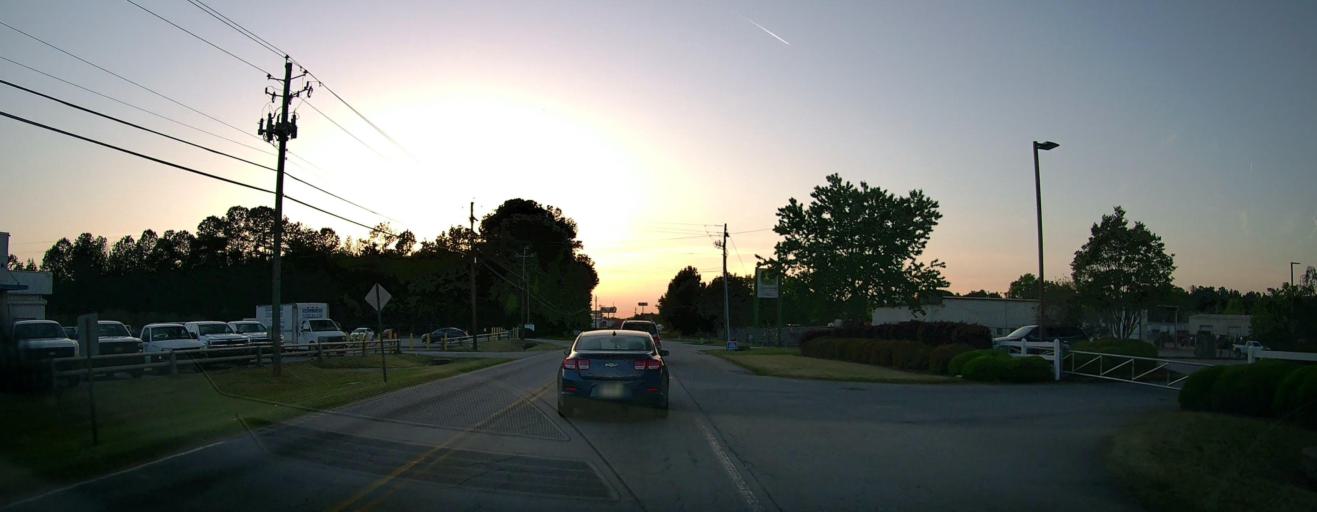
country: US
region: Georgia
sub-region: Henry County
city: McDonough
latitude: 33.4150
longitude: -84.1615
